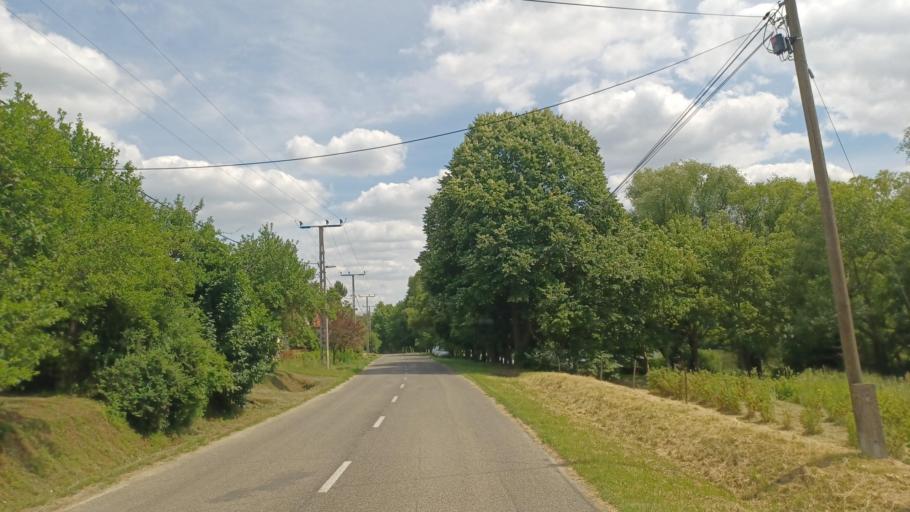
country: HU
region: Tolna
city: Simontornya
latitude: 46.6821
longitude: 18.5292
